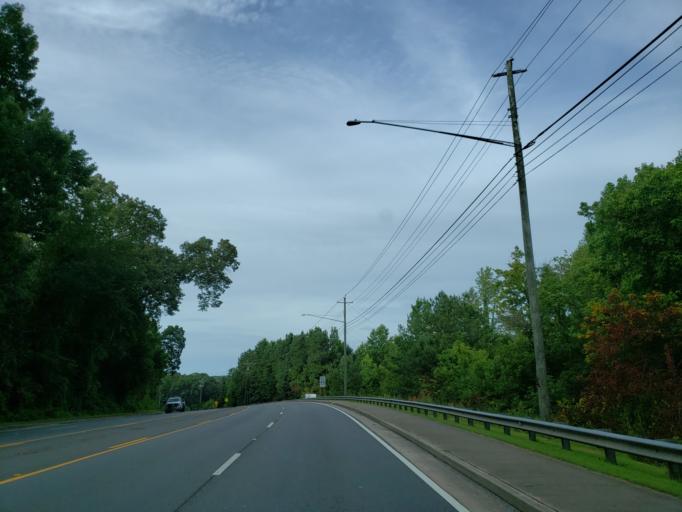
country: US
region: Georgia
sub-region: Cherokee County
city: Canton
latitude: 34.2389
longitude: -84.4988
